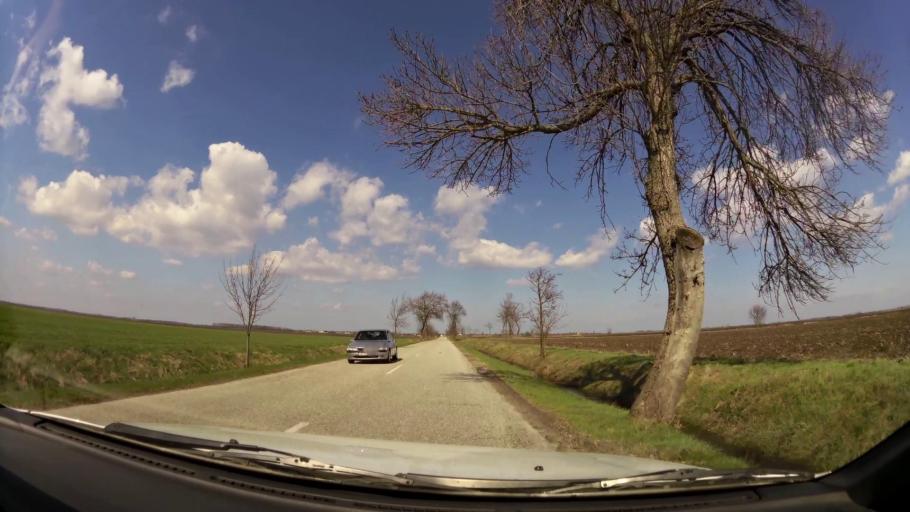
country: HU
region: Pest
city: Tapiogyorgye
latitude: 47.3085
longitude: 19.9423
